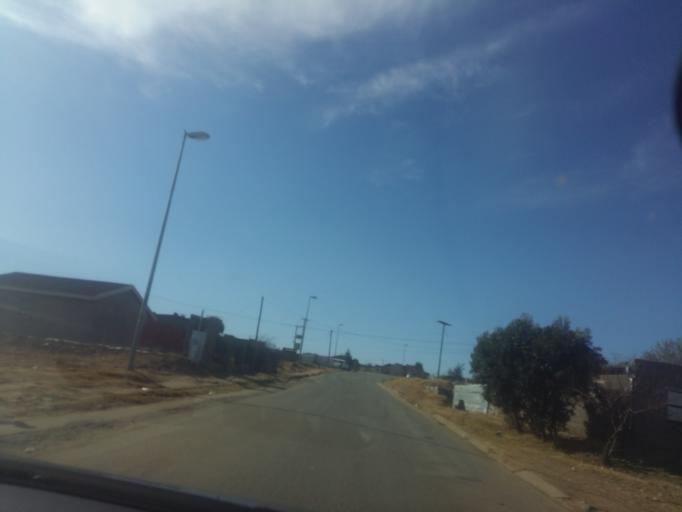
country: LS
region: Maseru
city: Maseru
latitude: -29.3938
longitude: 27.5201
